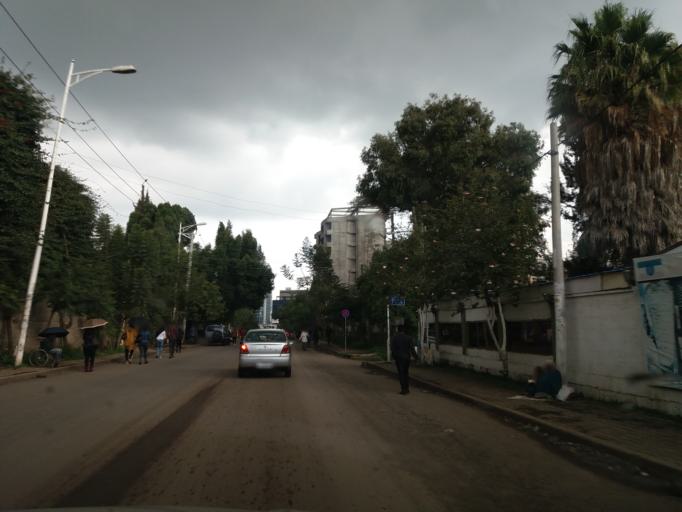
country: ET
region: Adis Abeba
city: Addis Ababa
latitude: 8.9929
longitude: 38.7849
